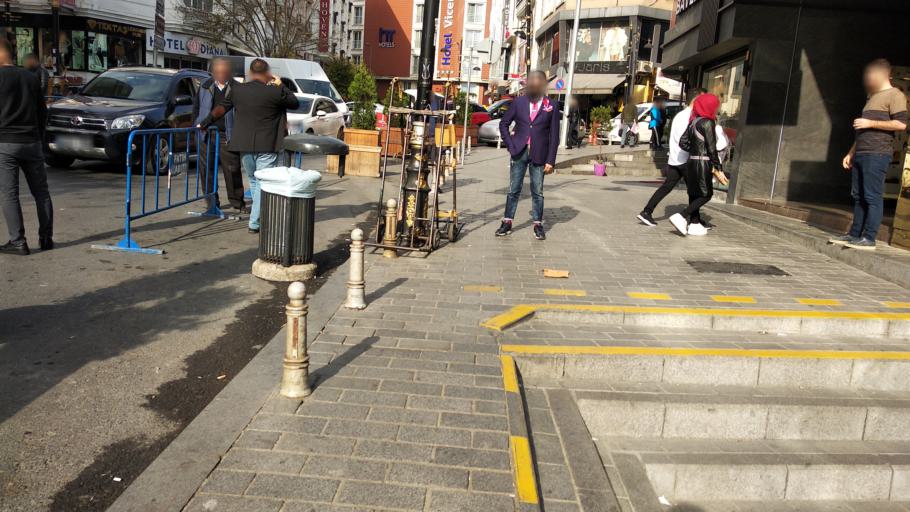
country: TR
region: Istanbul
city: Istanbul
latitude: 41.0112
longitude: 28.9574
